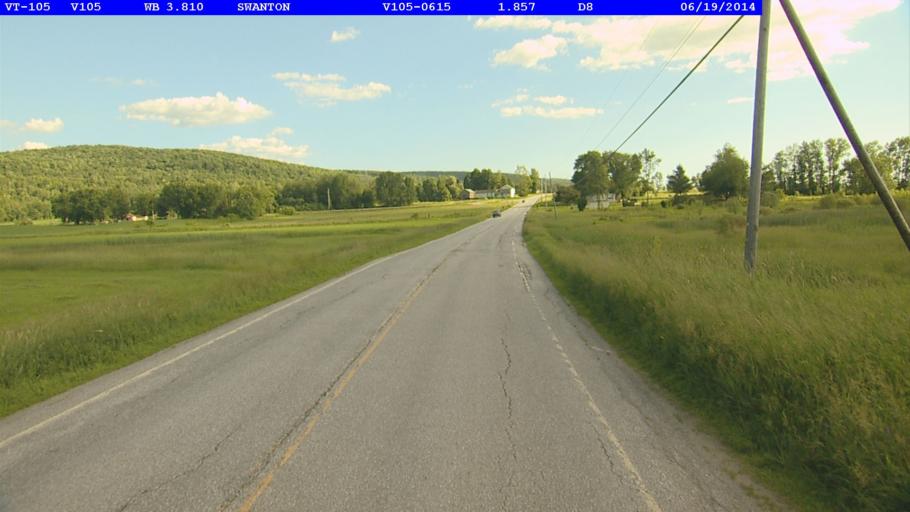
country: US
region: Vermont
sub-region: Franklin County
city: Saint Albans
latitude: 44.8592
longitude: -73.0325
